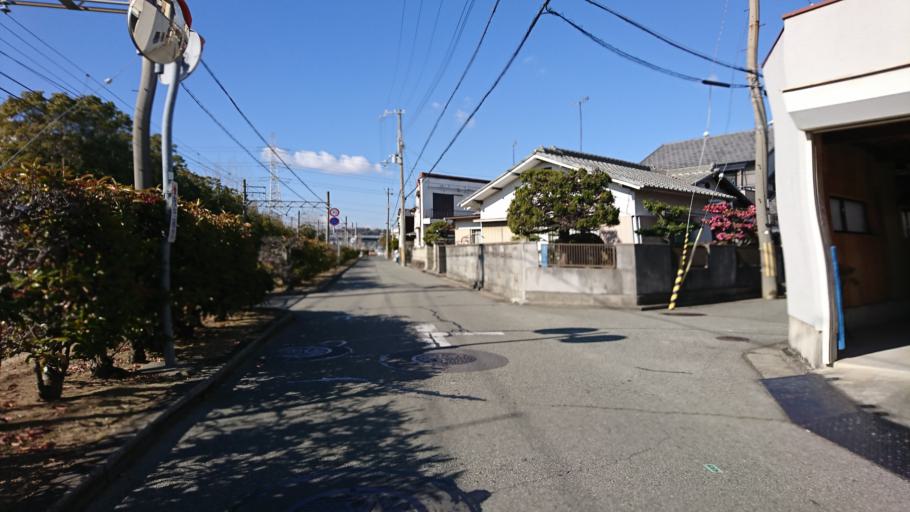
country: JP
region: Hyogo
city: Kakogawacho-honmachi
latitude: 34.7723
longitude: 134.7807
